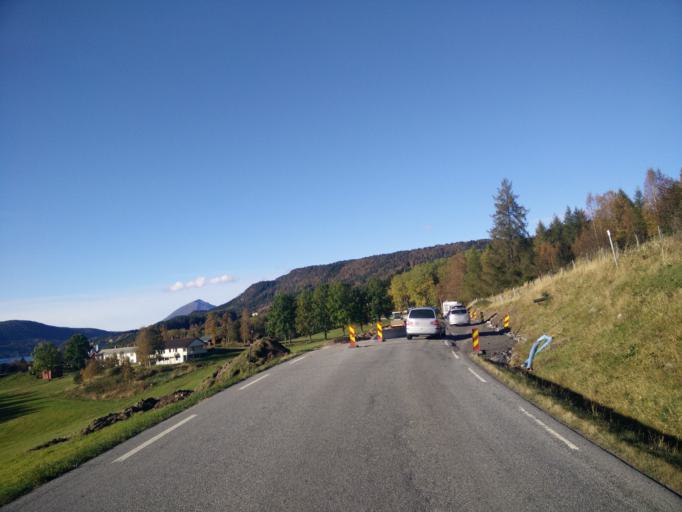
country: NO
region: More og Romsdal
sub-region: Halsa
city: Liaboen
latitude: 63.1115
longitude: 8.3271
